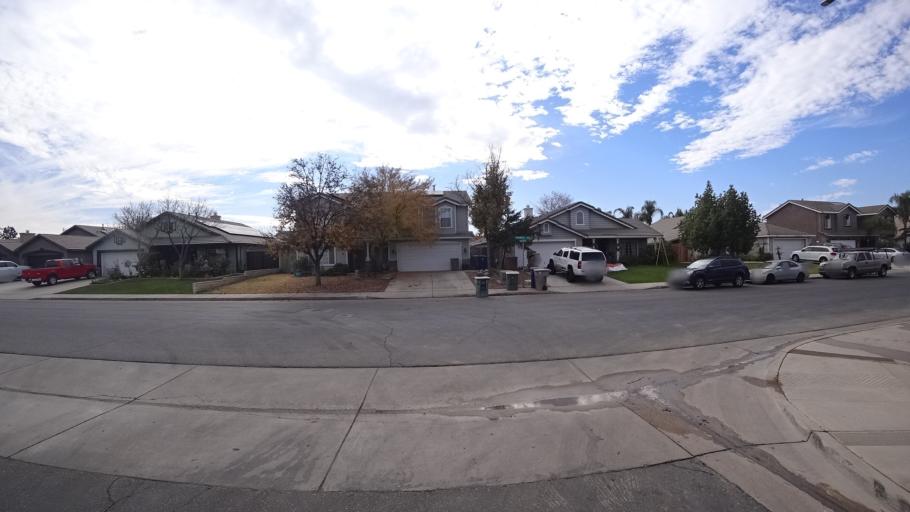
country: US
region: California
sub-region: Kern County
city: Rosedale
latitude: 35.4032
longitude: -119.1306
